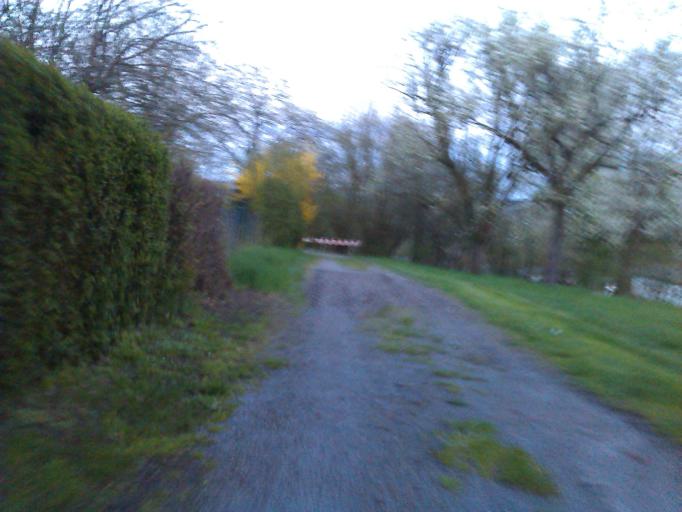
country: DE
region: Baden-Wuerttemberg
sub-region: Regierungsbezirk Stuttgart
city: Untereisesheim
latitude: 49.2114
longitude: 9.1841
